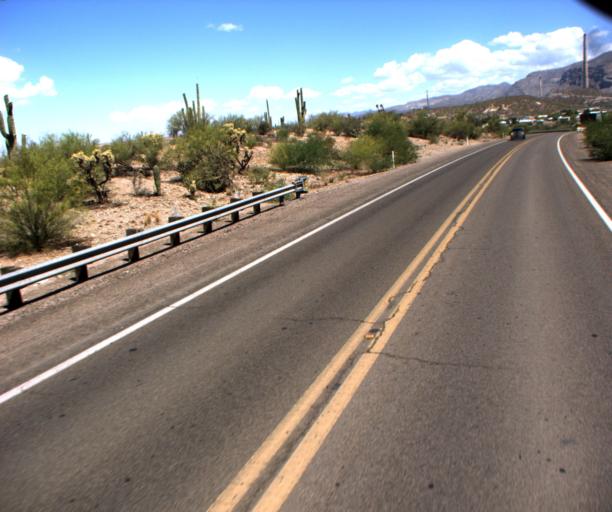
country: US
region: Arizona
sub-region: Pinal County
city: Kearny
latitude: 32.9794
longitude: -110.7690
